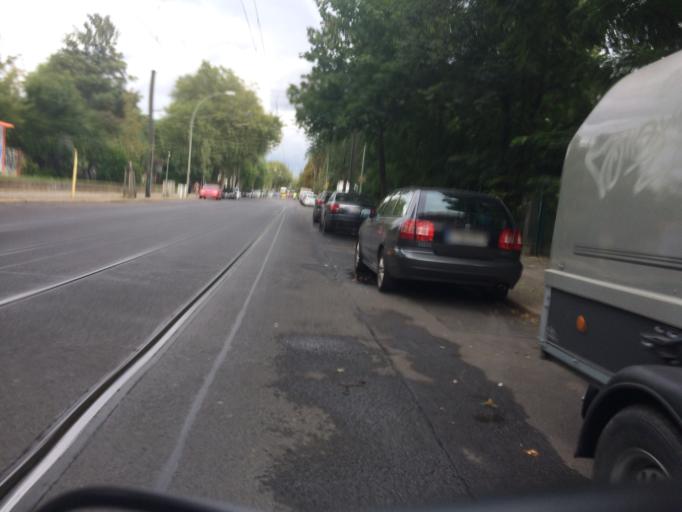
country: DE
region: Berlin
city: Lichtenberg
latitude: 52.5265
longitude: 13.4922
